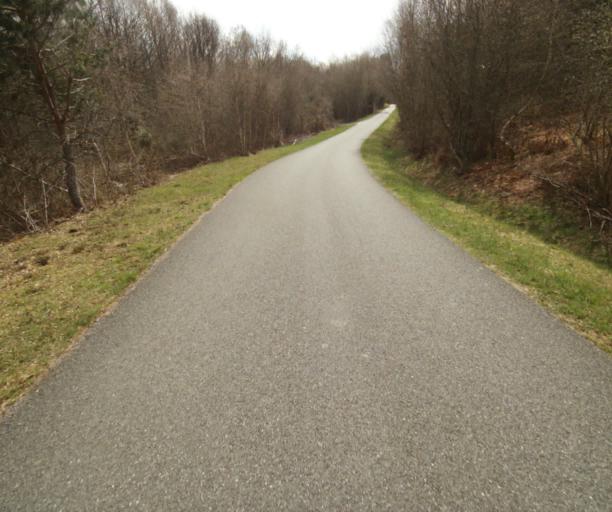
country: FR
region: Limousin
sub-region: Departement de la Correze
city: Egletons
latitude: 45.3730
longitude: 1.9662
